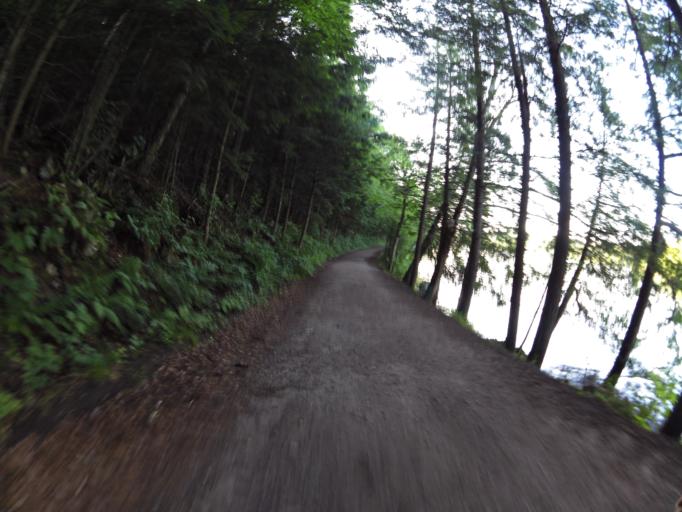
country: CA
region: Quebec
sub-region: Outaouais
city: Wakefield
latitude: 45.5900
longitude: -75.9837
